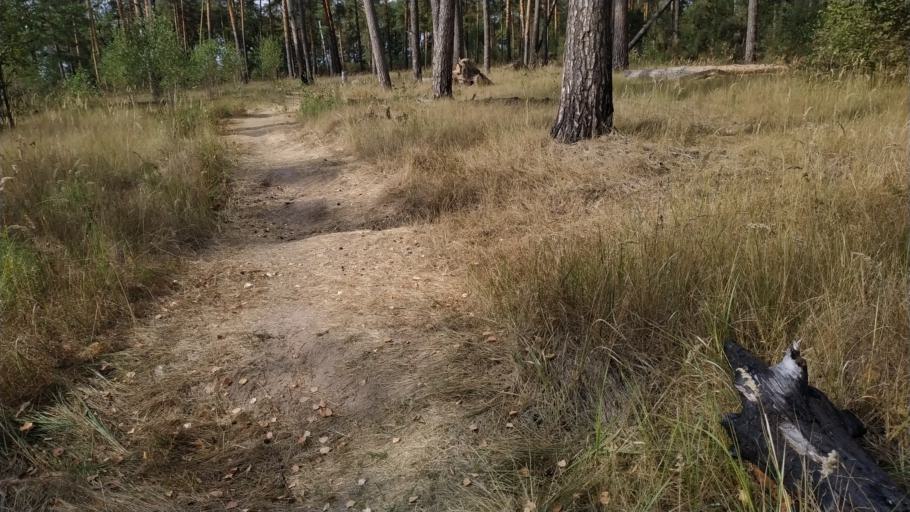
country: RU
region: Moskovskaya
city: Ramenskoye
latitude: 55.5345
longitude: 38.2915
